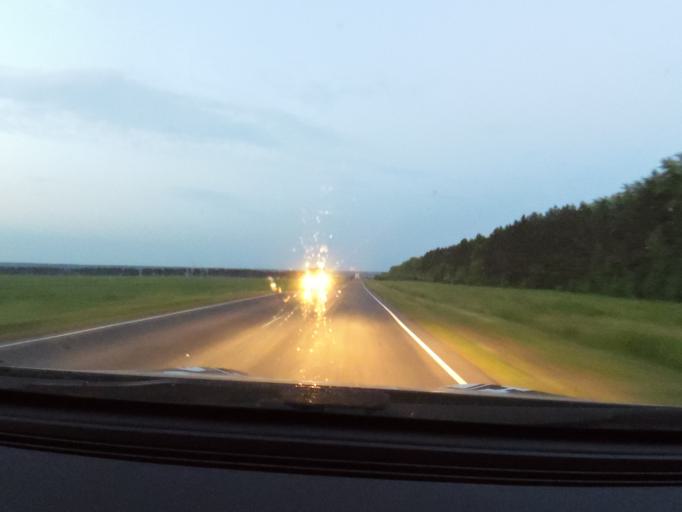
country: RU
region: Bashkortostan
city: Duvan
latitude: 56.0761
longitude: 58.1355
